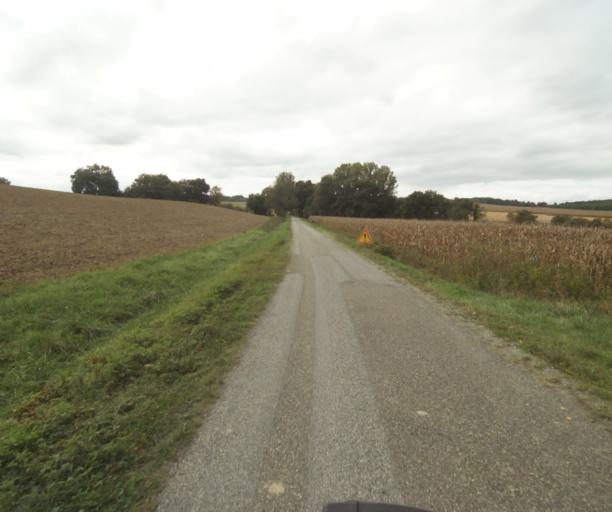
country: FR
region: Midi-Pyrenees
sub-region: Departement du Tarn-et-Garonne
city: Beaumont-de-Lomagne
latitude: 43.8306
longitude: 1.0678
